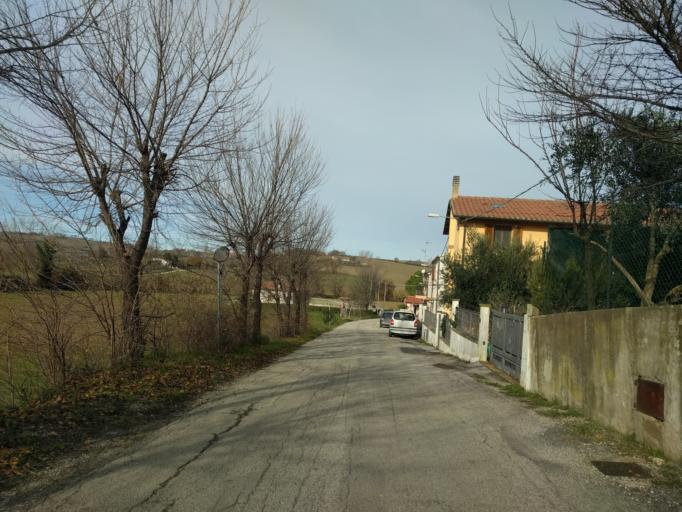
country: IT
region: The Marches
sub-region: Provincia di Pesaro e Urbino
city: Cuccurano
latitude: 43.7984
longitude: 12.9475
